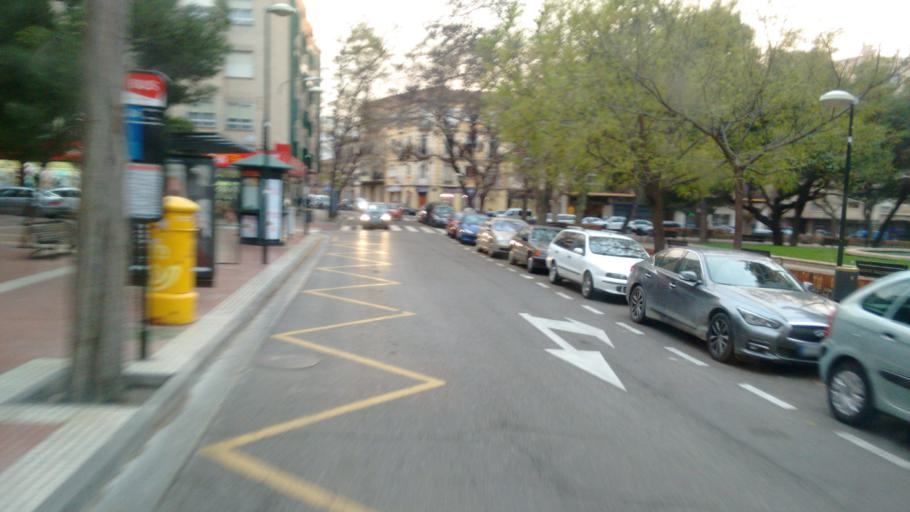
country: ES
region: Aragon
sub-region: Provincia de Zaragoza
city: Zaragoza
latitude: 41.6609
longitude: -0.8760
